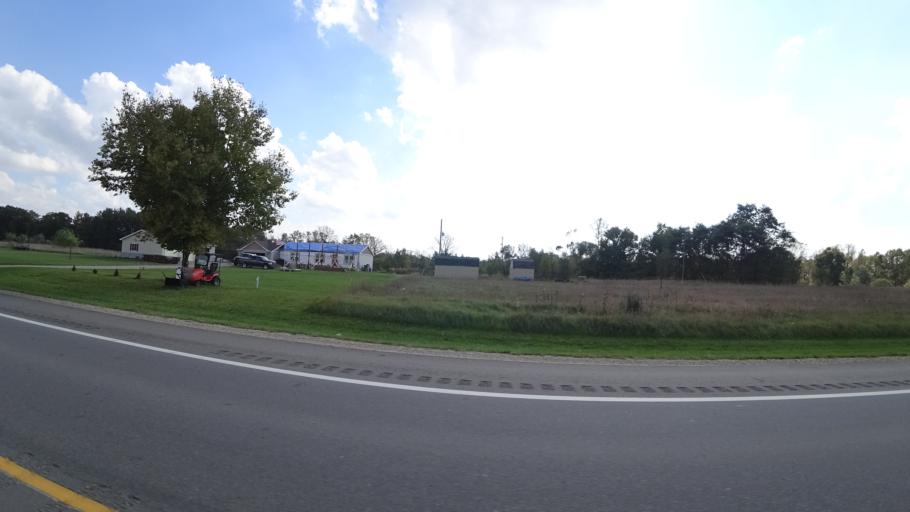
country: US
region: Michigan
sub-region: Calhoun County
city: Athens
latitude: 42.0619
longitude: -85.2520
